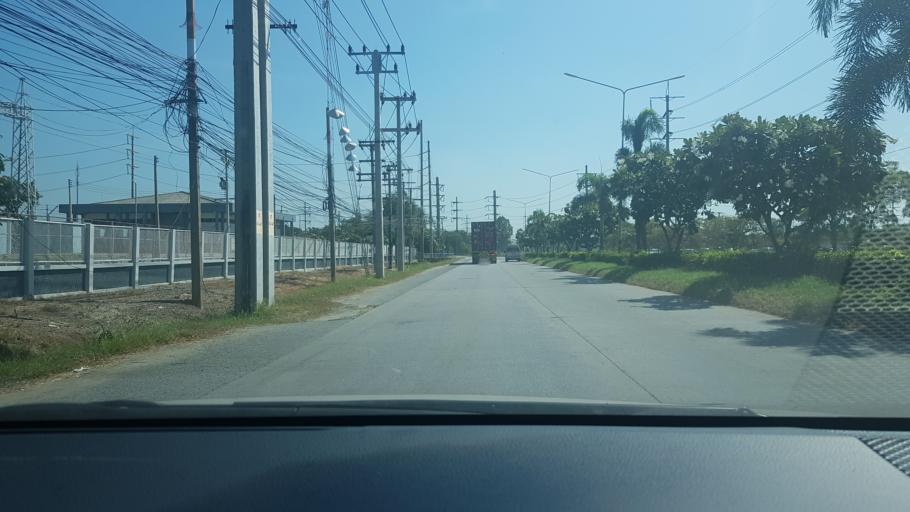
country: TH
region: Phra Nakhon Si Ayutthaya
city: Bang Pa-in
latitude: 14.2501
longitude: 100.6095
